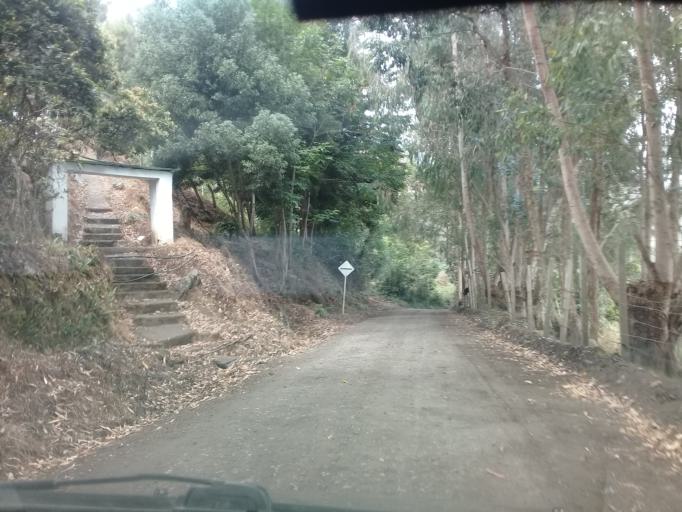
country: CO
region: Cundinamarca
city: Une
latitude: 4.4048
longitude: -73.9910
